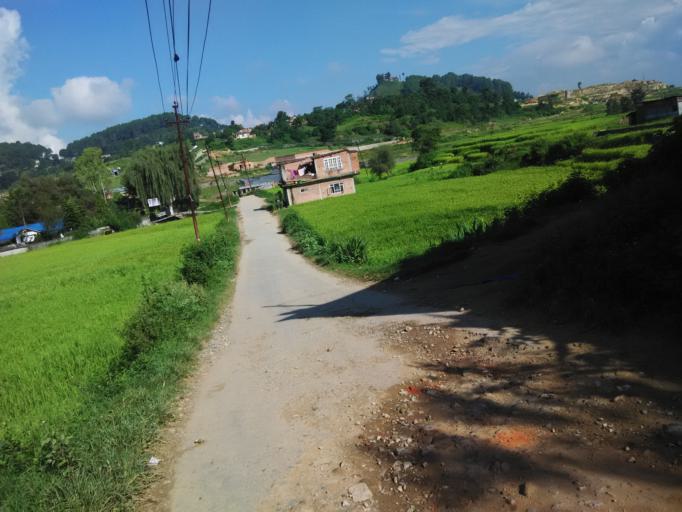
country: NP
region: Central Region
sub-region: Bagmati Zone
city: Patan
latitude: 27.6061
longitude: 85.3503
